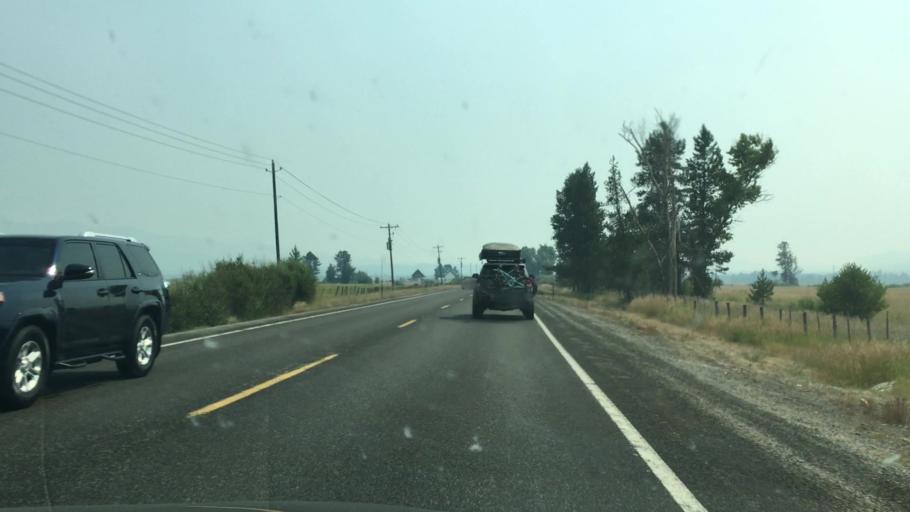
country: US
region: Idaho
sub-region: Valley County
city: Cascade
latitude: 44.4315
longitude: -115.9998
